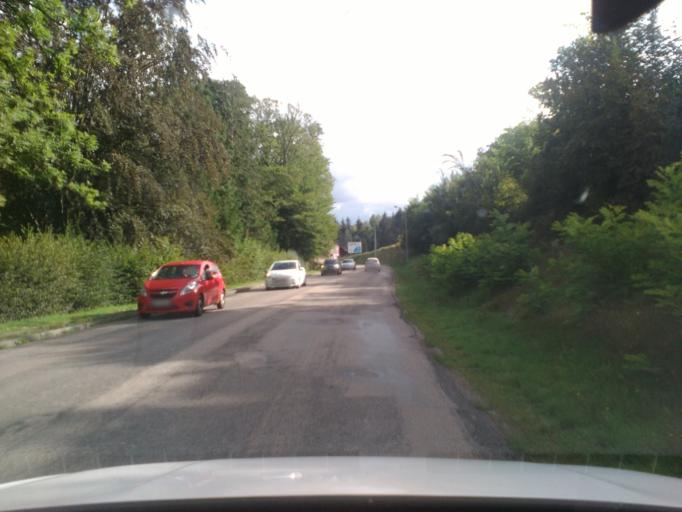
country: FR
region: Lorraine
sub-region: Departement des Vosges
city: Saint-Die-des-Vosges
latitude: 48.2669
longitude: 6.9613
